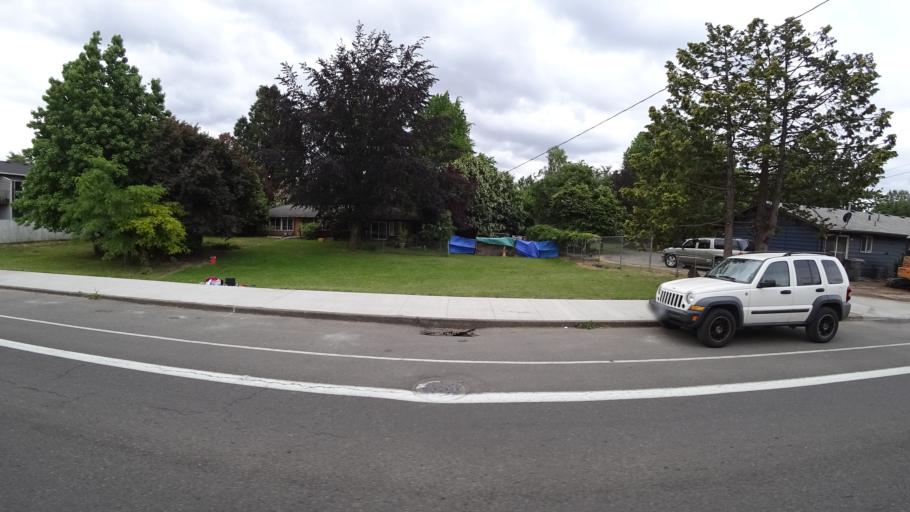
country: US
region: Oregon
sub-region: Multnomah County
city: Lents
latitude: 45.4685
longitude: -122.5706
